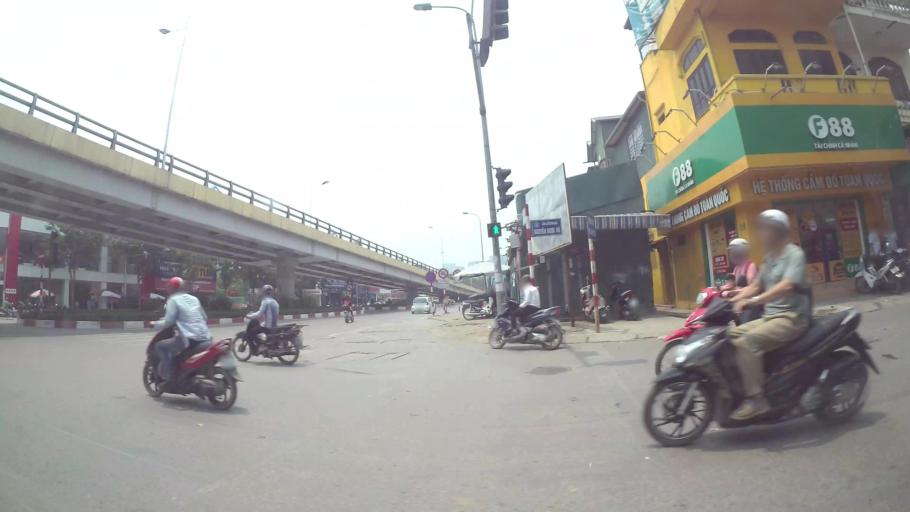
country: VN
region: Ha Noi
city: Thanh Xuan
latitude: 21.0104
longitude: 105.8105
